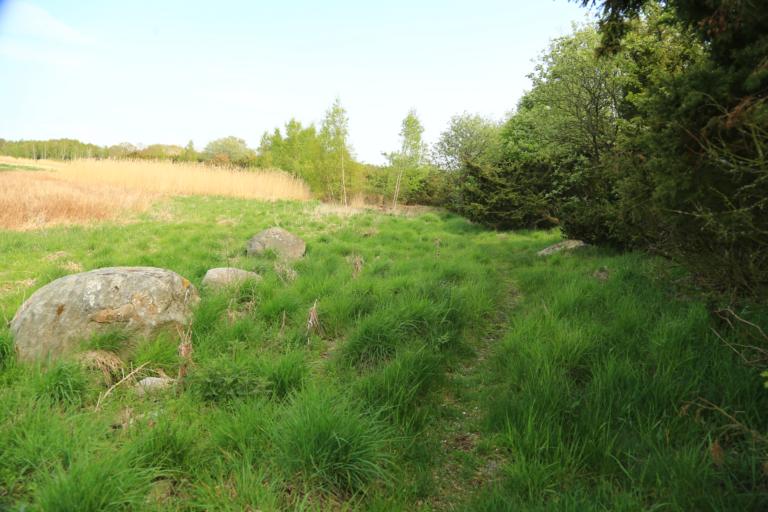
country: SE
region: Halland
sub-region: Varbergs Kommun
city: Varberg
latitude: 57.1524
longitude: 12.2162
